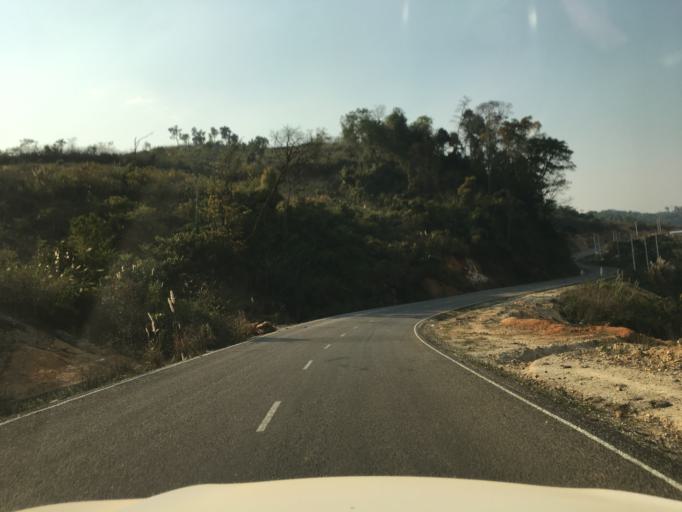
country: LA
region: Houaphan
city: Xam Nua
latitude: 20.5708
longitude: 104.0581
